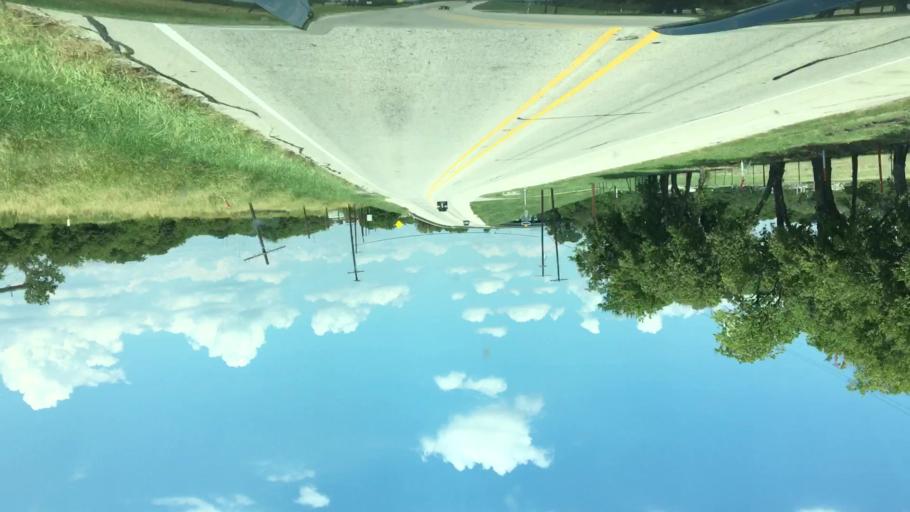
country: US
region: Texas
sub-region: Tarrant County
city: Haslet
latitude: 32.9759
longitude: -97.3462
